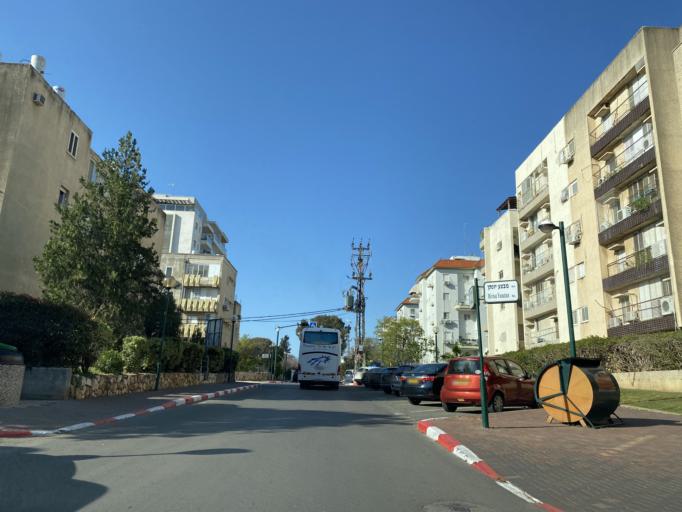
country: IL
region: Central District
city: Kfar Saba
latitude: 32.1794
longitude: 34.9156
